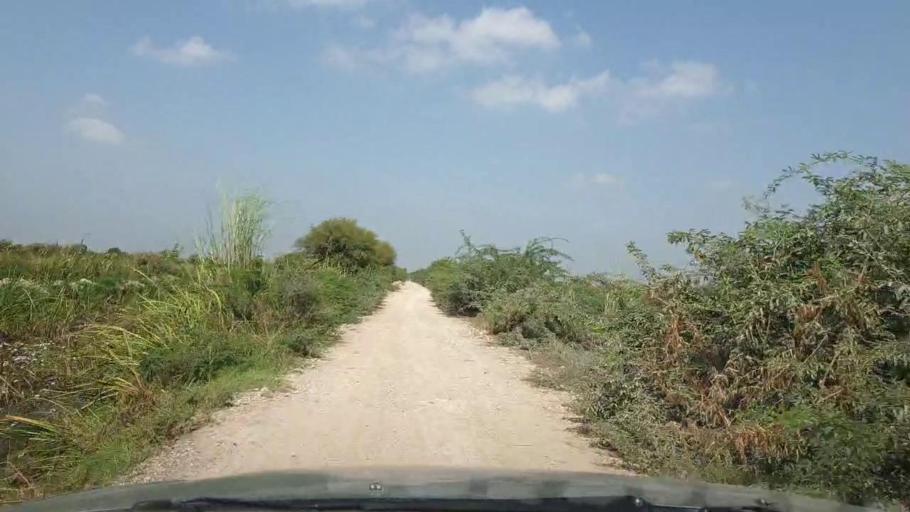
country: PK
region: Sindh
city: Rajo Khanani
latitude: 25.0202
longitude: 68.9165
